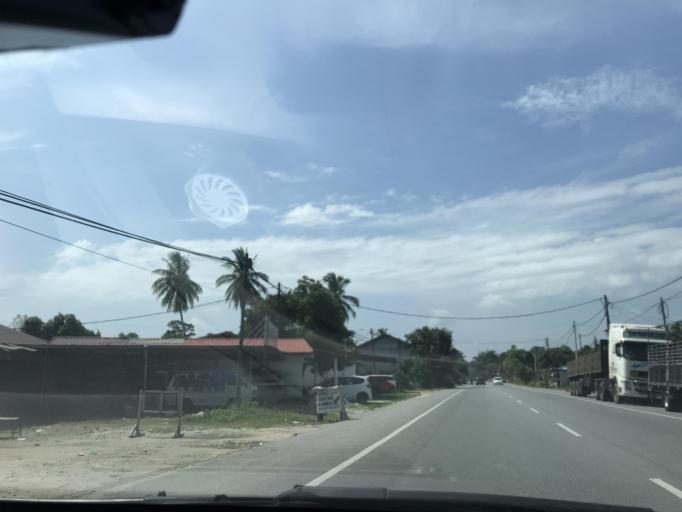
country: MY
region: Kelantan
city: Tumpat
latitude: 6.1418
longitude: 102.1675
